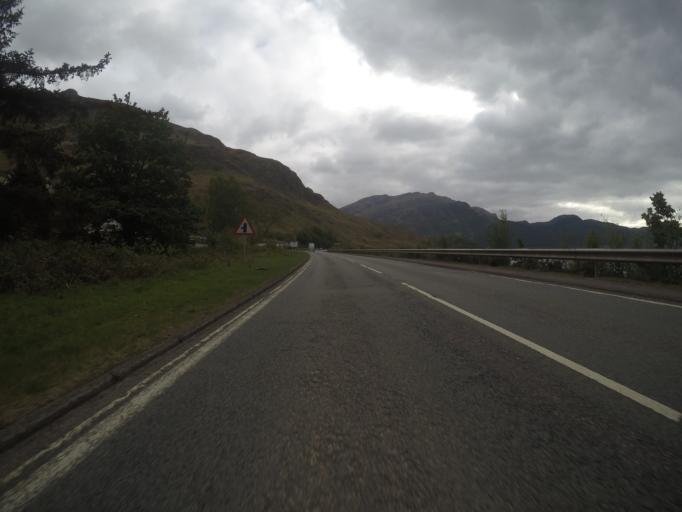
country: GB
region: Scotland
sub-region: Highland
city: Fort William
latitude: 57.2274
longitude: -5.4060
